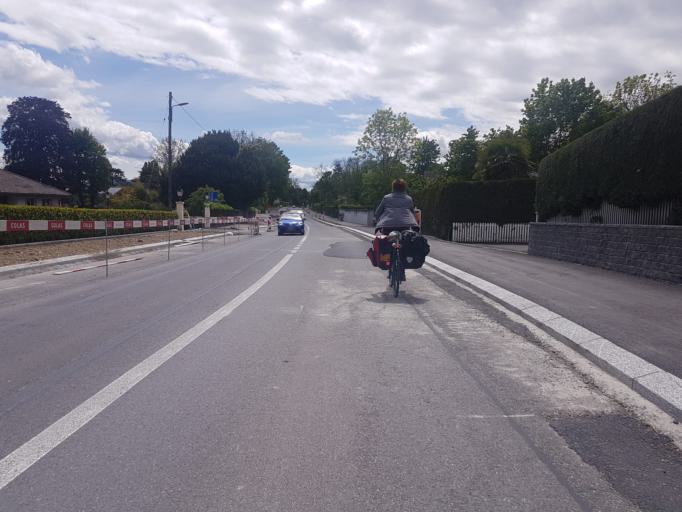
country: CH
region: Vaud
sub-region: Nyon District
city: Founex
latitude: 46.3267
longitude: 6.1991
